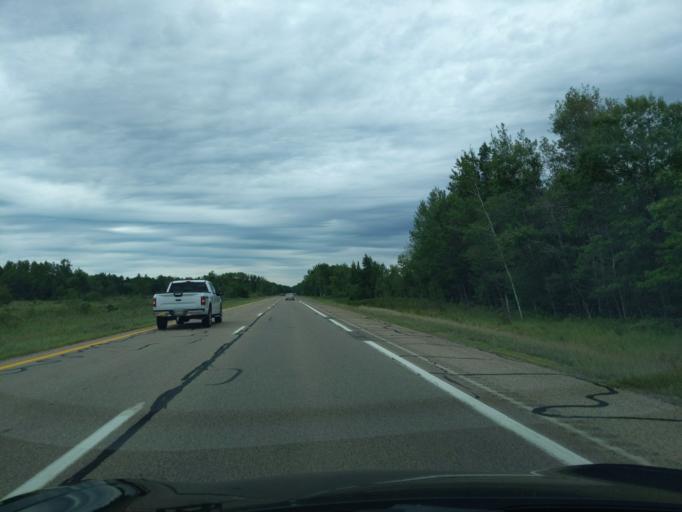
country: US
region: Michigan
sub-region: Roscommon County
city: Houghton Lake
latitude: 44.2885
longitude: -84.8009
